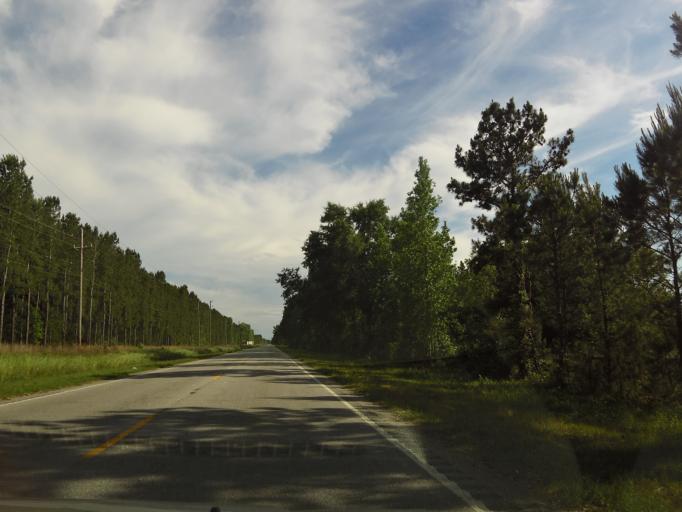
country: US
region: South Carolina
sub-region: Allendale County
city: Fairfax
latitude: 32.9306
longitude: -81.2372
